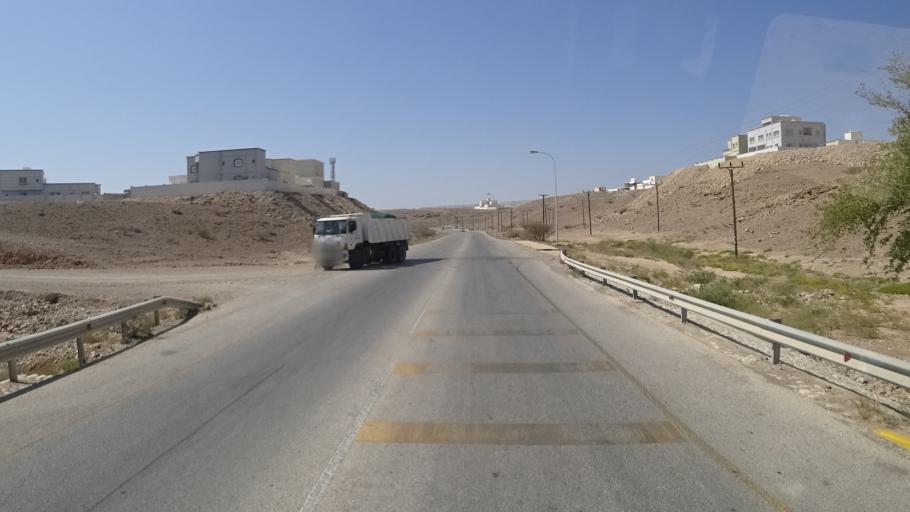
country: OM
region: Ash Sharqiyah
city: Sur
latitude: 22.5523
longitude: 59.4985
